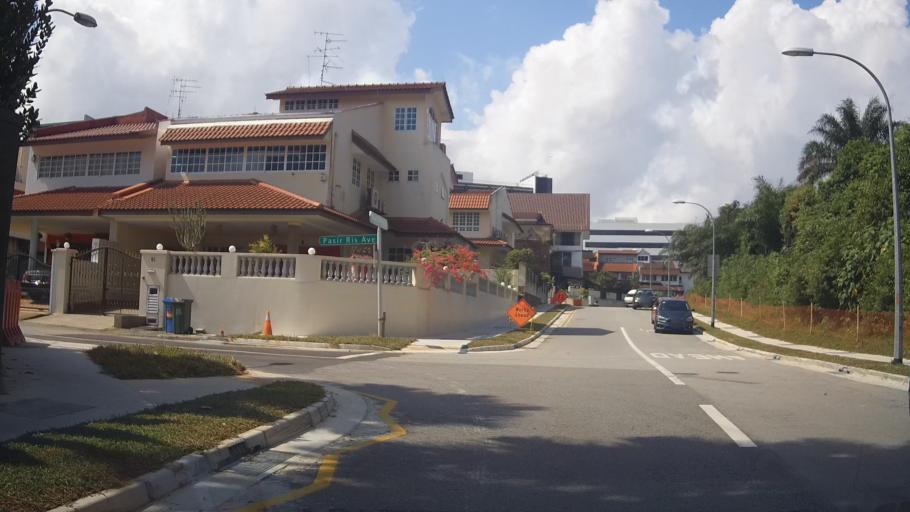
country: MY
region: Johor
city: Kampung Pasir Gudang Baru
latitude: 1.3835
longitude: 103.9432
